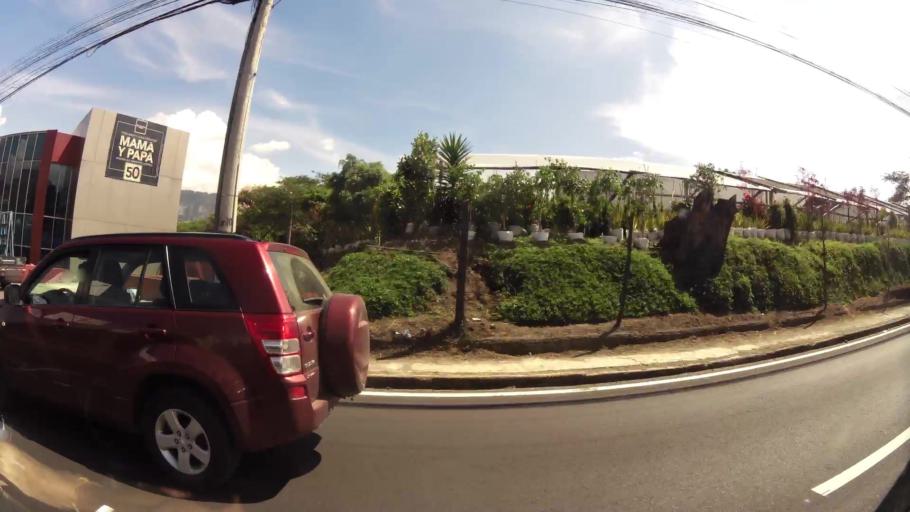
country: EC
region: Pichincha
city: Quito
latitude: -0.2110
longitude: -78.4218
